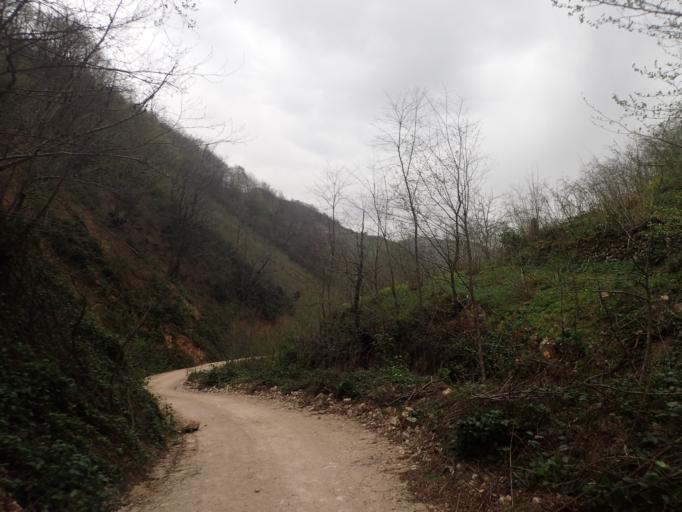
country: TR
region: Ordu
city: Kabaduz
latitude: 40.7882
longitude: 37.8940
